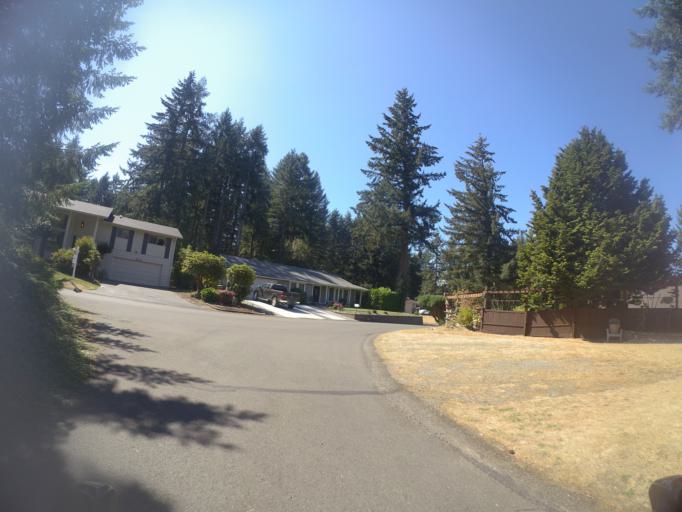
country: US
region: Washington
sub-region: Pierce County
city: University Place
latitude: 47.2150
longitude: -122.5563
